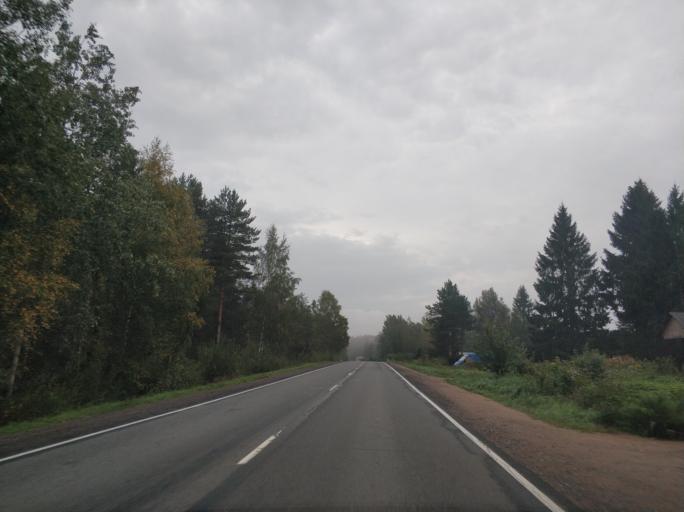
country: RU
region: Leningrad
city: Shcheglovo
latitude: 60.0952
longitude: 30.8478
